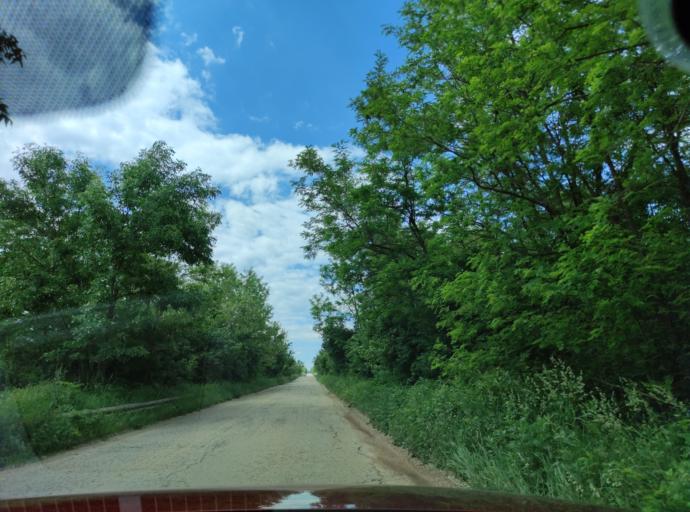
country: BG
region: Montana
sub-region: Obshtina Berkovitsa
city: Berkovitsa
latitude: 43.3601
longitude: 23.0912
